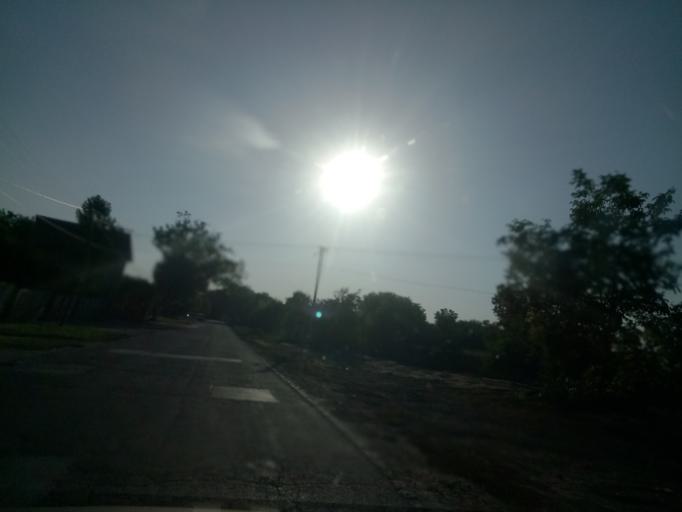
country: RS
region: Autonomna Pokrajina Vojvodina
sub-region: Sremski Okrug
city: Stara Pazova
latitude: 44.9968
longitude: 20.1610
